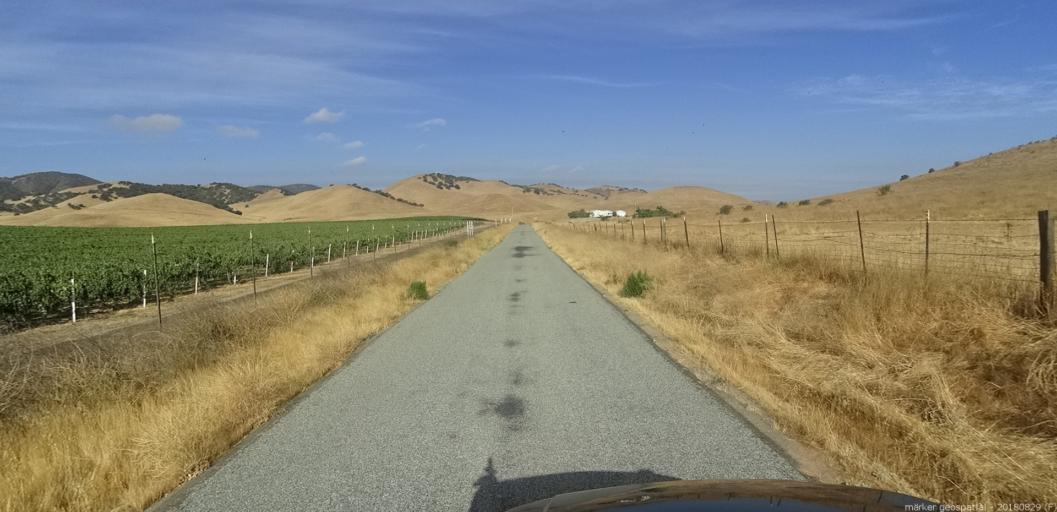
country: US
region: California
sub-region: Monterey County
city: King City
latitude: 36.0181
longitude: -120.9446
